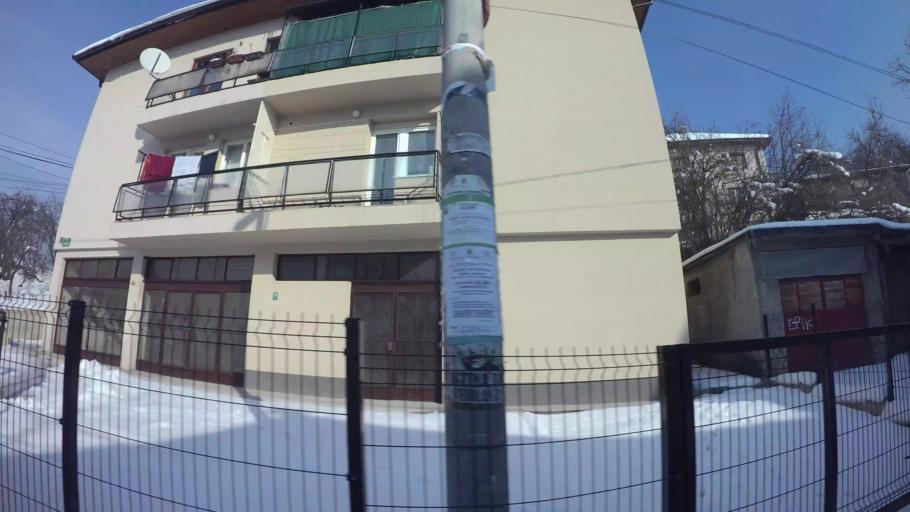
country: BA
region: Federation of Bosnia and Herzegovina
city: Kobilja Glava
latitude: 43.8479
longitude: 18.4030
